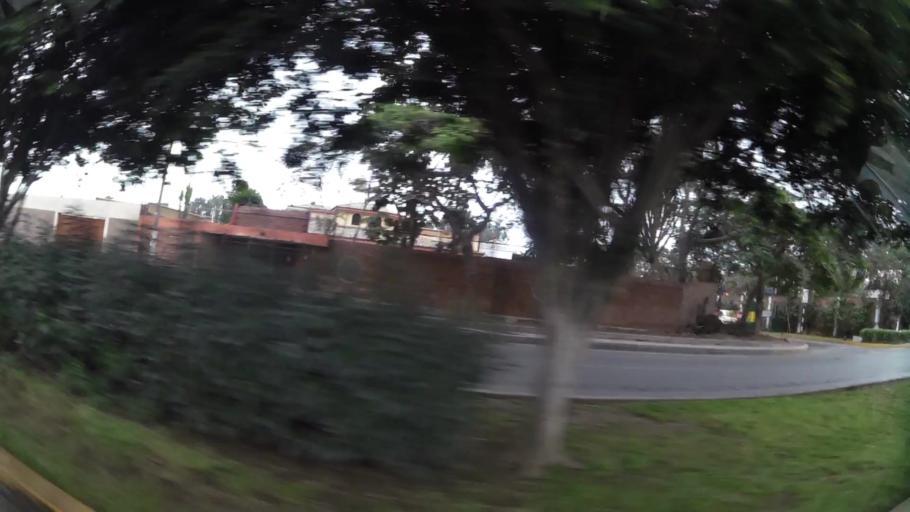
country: PE
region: Lima
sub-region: Lima
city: La Molina
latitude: -12.0689
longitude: -76.9646
